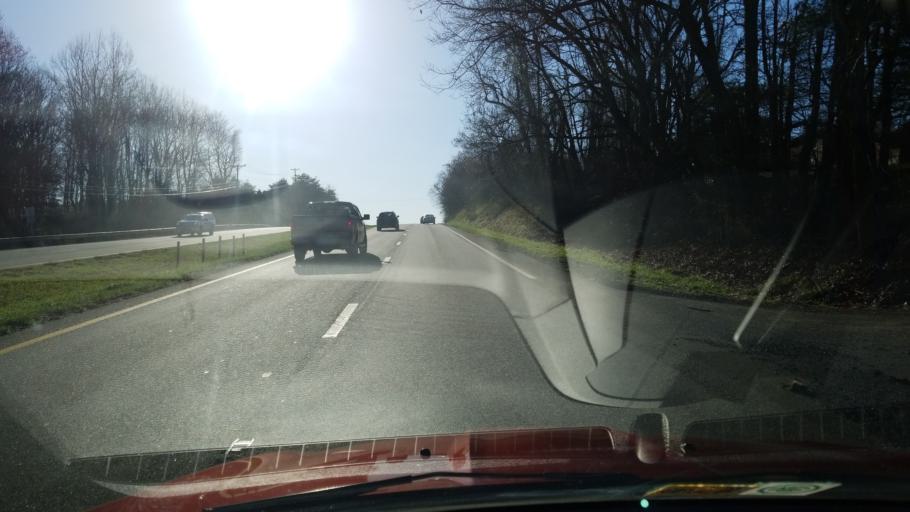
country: US
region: Virginia
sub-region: Franklin County
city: Rocky Mount
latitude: 37.0864
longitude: -79.9305
